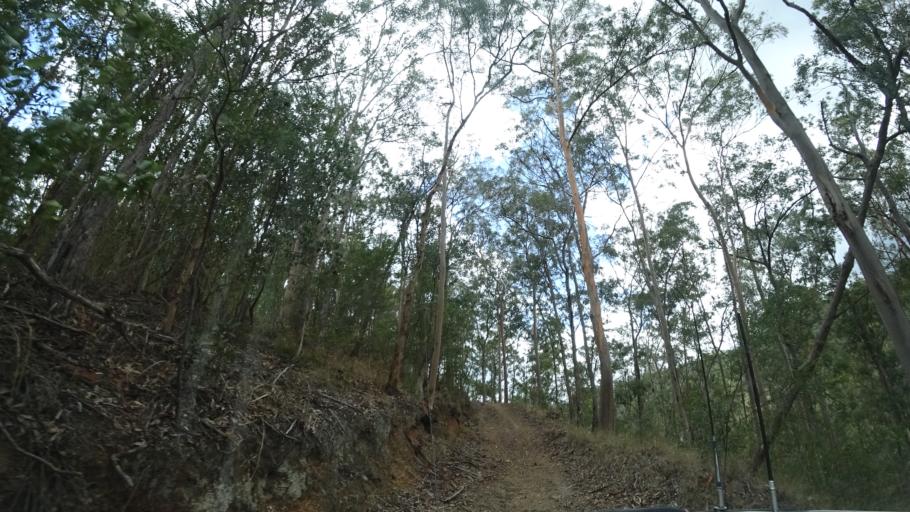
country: AU
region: Queensland
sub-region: Moreton Bay
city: Highvale
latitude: -27.4108
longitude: 152.7400
